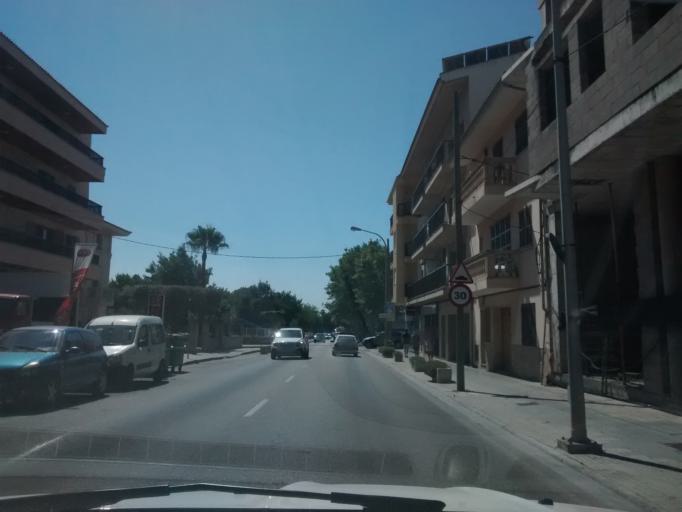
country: ES
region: Balearic Islands
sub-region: Illes Balears
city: Alcudia
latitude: 39.8495
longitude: 3.1276
